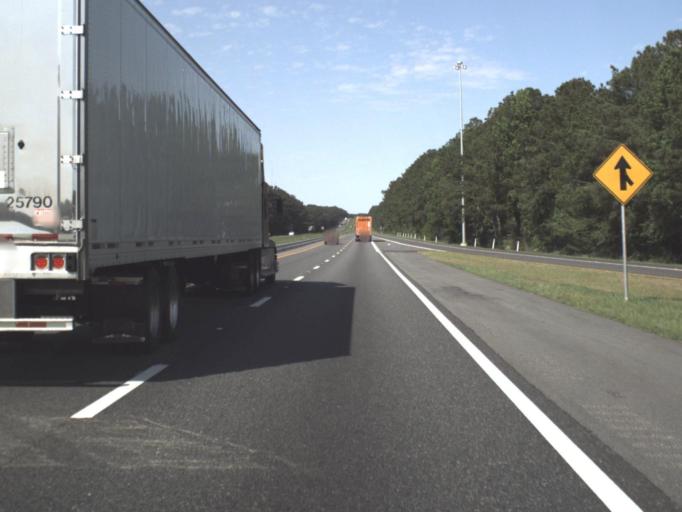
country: US
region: Florida
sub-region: Walton County
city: DeFuniak Springs
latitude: 30.7125
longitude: -85.9384
